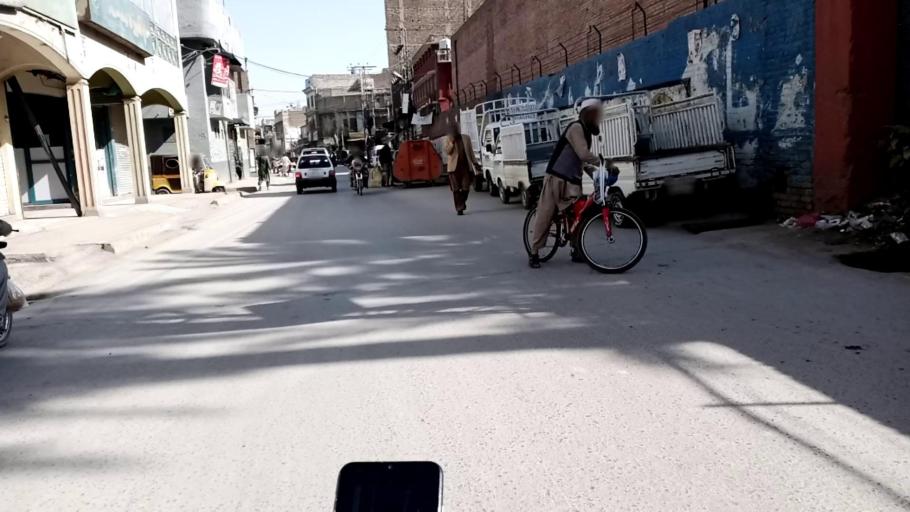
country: PK
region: Khyber Pakhtunkhwa
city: Peshawar
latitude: 34.0073
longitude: 71.5831
